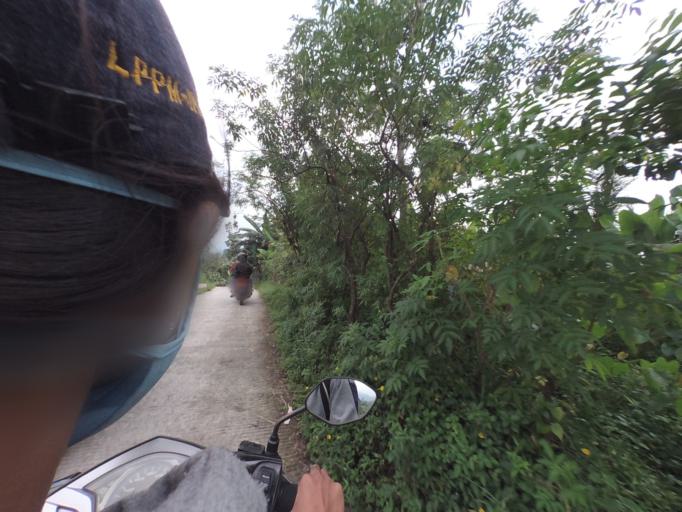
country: ID
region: West Java
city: Ciampea
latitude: -6.6909
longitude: 106.6547
